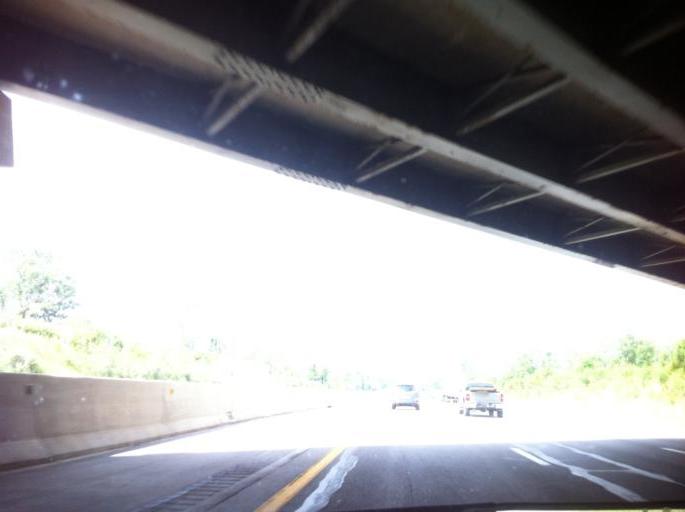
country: US
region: Ohio
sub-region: Portage County
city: Streetsboro
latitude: 41.2560
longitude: -81.3714
